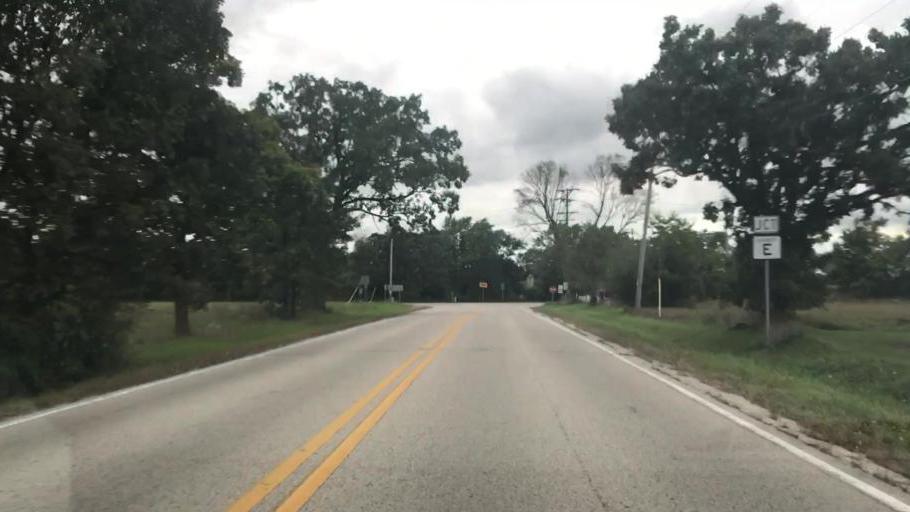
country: US
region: Wisconsin
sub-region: Waukesha County
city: North Prairie
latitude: 42.9072
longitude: -88.4076
